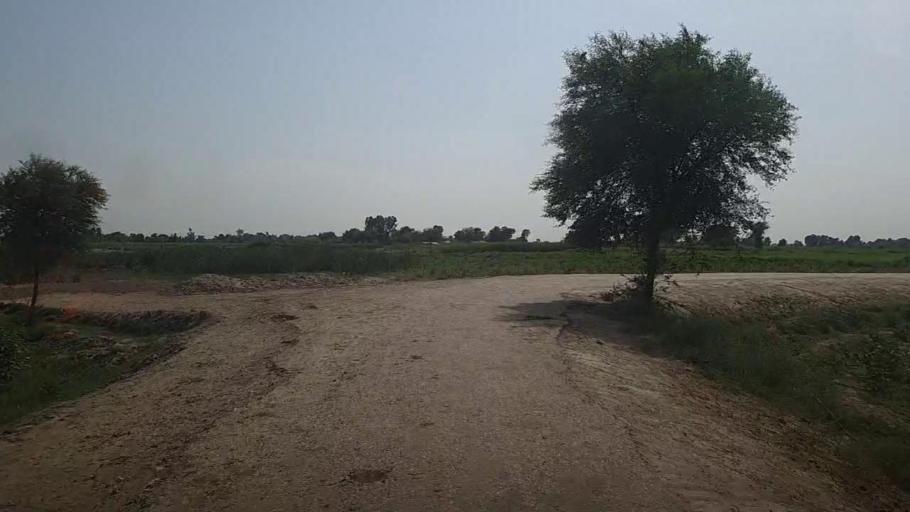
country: PK
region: Sindh
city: Ubauro
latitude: 28.1457
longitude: 69.8009
